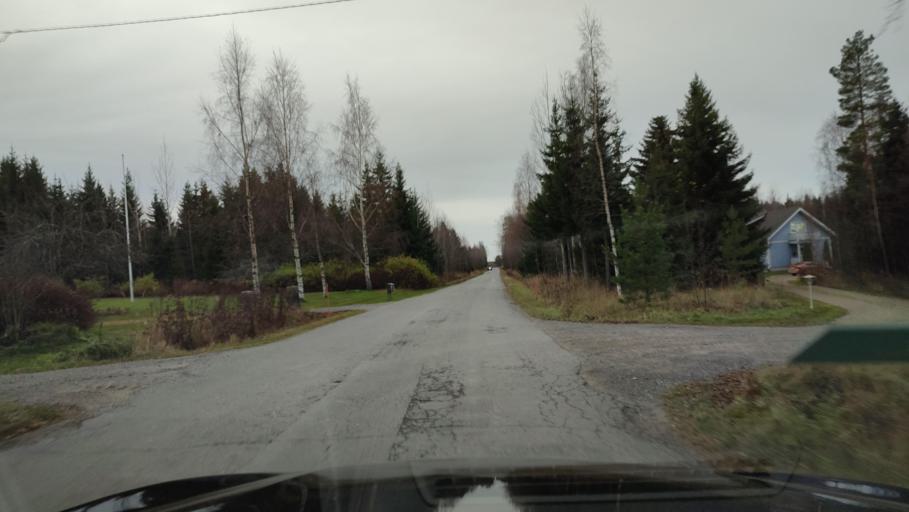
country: FI
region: Ostrobothnia
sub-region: Sydosterbotten
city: Naerpes
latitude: 62.4264
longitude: 21.4166
